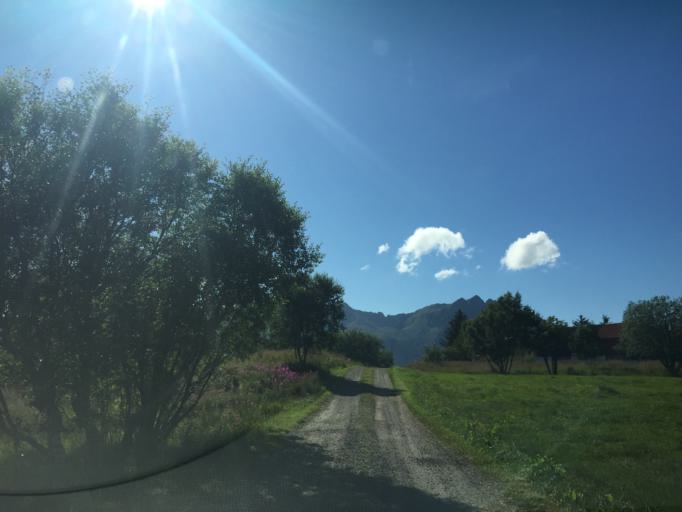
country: NO
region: Nordland
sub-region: Vagan
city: Kabelvag
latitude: 68.3518
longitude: 14.4596
